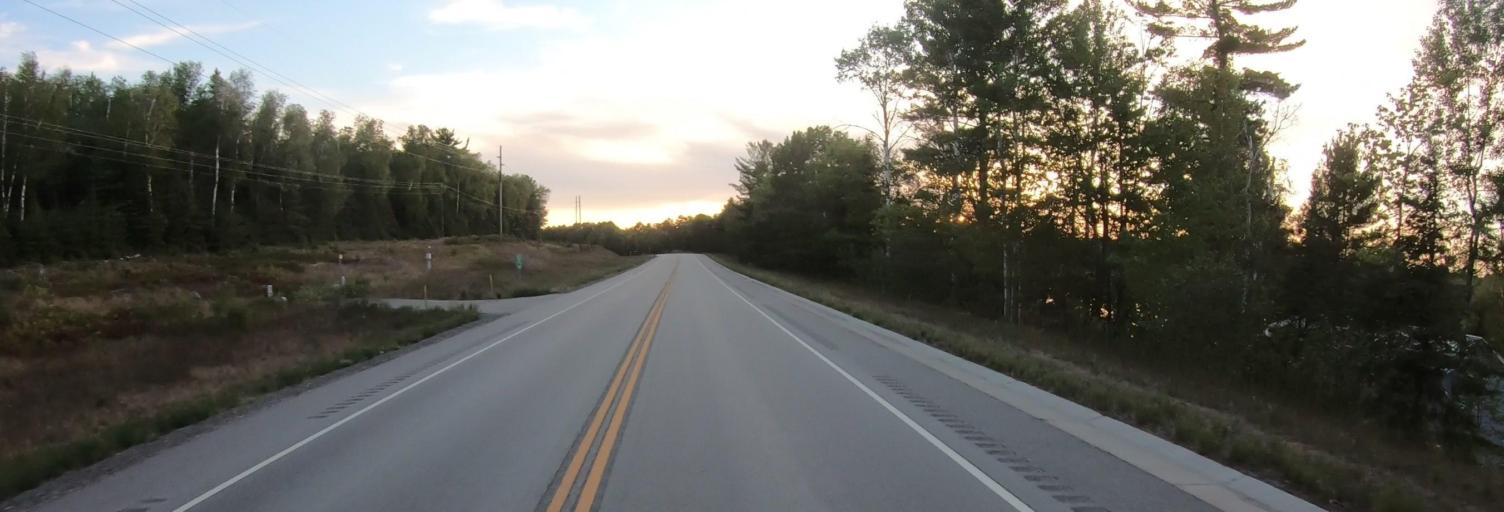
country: US
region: Minnesota
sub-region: Saint Louis County
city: Babbitt
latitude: 47.8573
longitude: -92.0727
